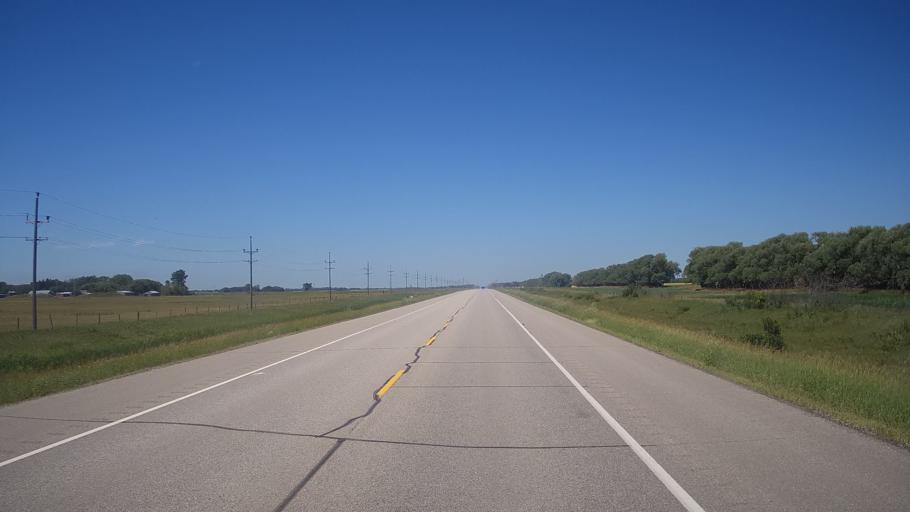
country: CA
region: Manitoba
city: Neepawa
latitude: 50.2257
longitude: -99.0558
